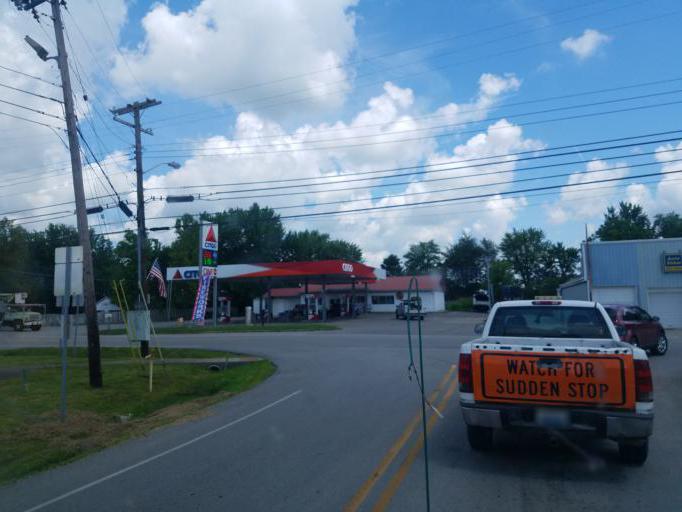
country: US
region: Kentucky
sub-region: Grayson County
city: Leitchfield
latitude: 37.4952
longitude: -86.2254
